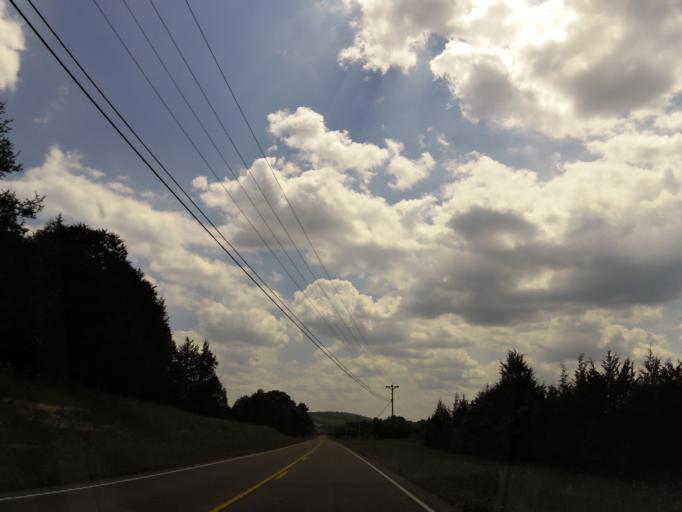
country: US
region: Tennessee
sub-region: Bledsoe County
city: Pikeville
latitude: 35.5527
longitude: -85.2530
